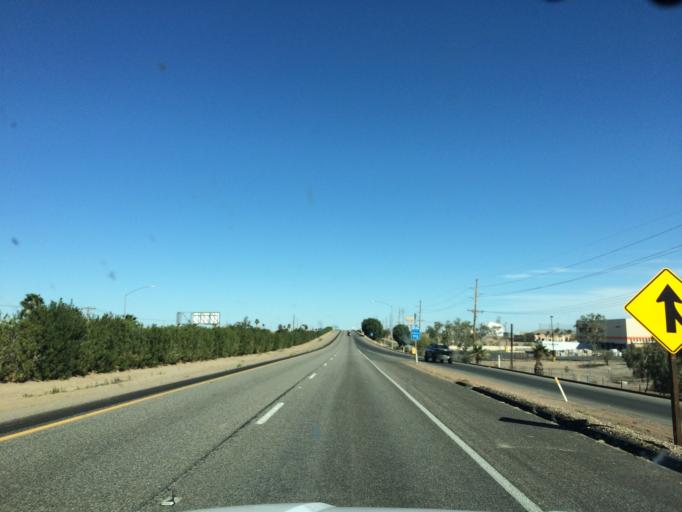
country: US
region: California
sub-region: Imperial County
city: El Centro
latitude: 32.7737
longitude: -115.5503
